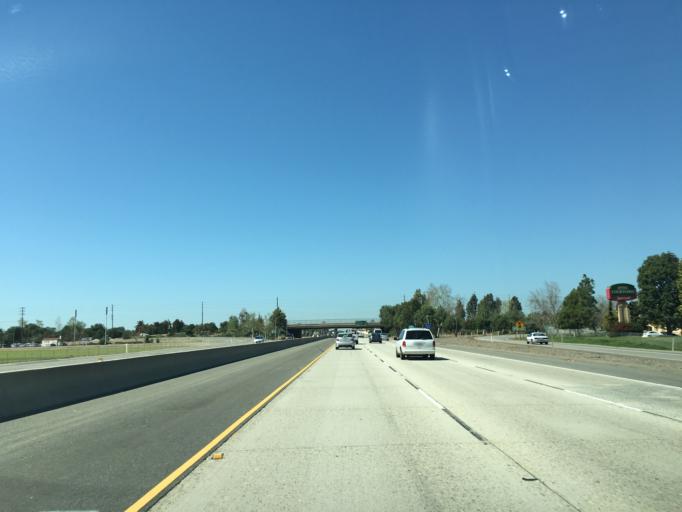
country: US
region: California
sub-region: Ventura County
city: Camarillo
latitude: 34.2127
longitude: -119.0044
